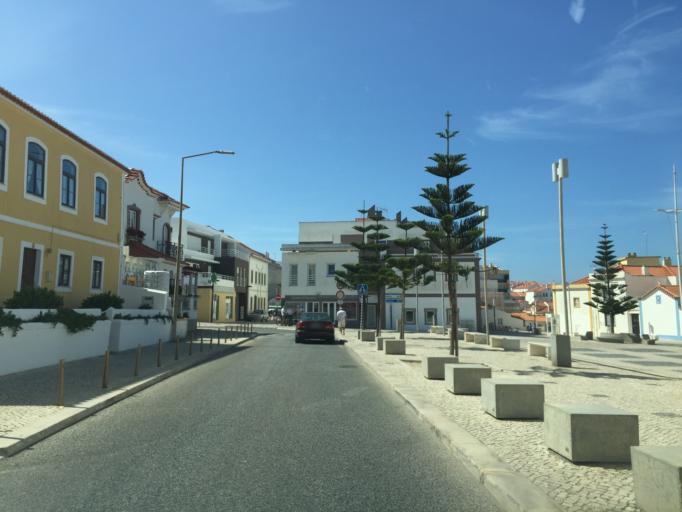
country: PT
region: Lisbon
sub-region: Torres Vedras
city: Silveira
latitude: 39.1354
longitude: -9.3815
